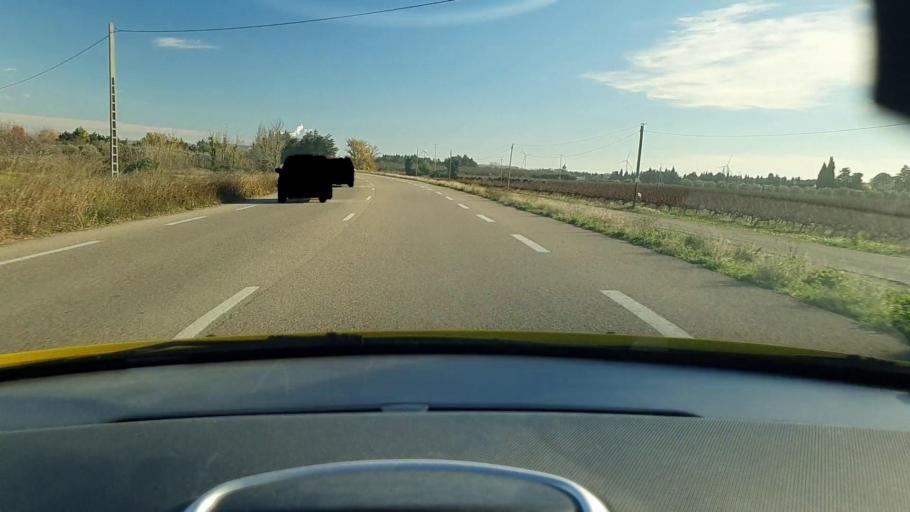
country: FR
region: Languedoc-Roussillon
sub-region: Departement du Gard
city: Beaucaire
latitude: 43.7934
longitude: 4.6126
